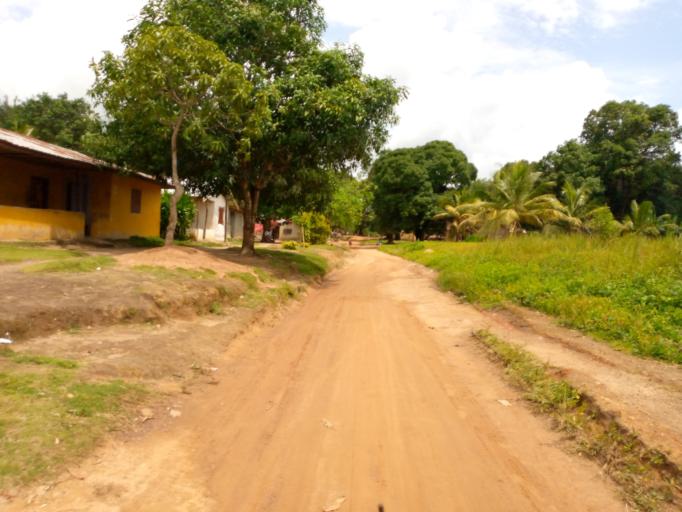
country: SL
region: Northern Province
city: Magburaka
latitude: 8.7082
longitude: -11.9643
